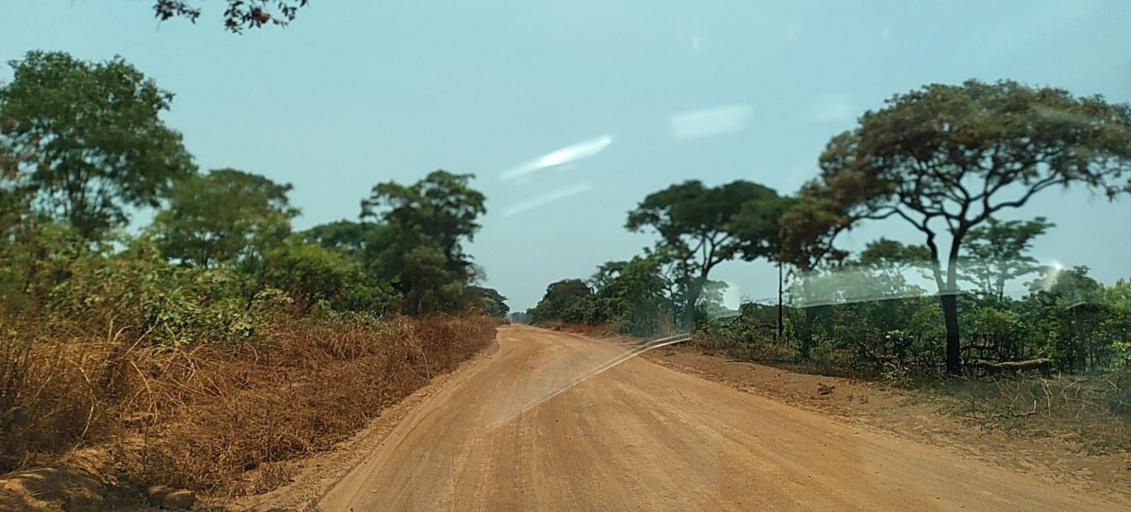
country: CD
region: Katanga
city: Kipushi
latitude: -11.9293
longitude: 26.9887
